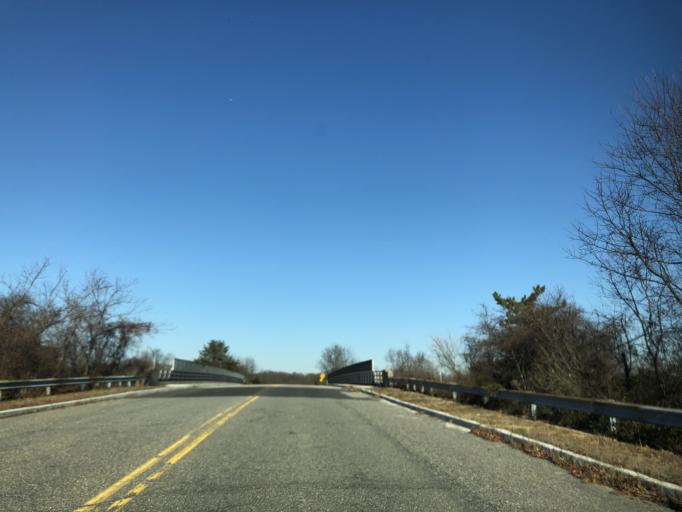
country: US
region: Pennsylvania
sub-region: Delaware County
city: Chester
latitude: 39.8021
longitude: -75.3414
